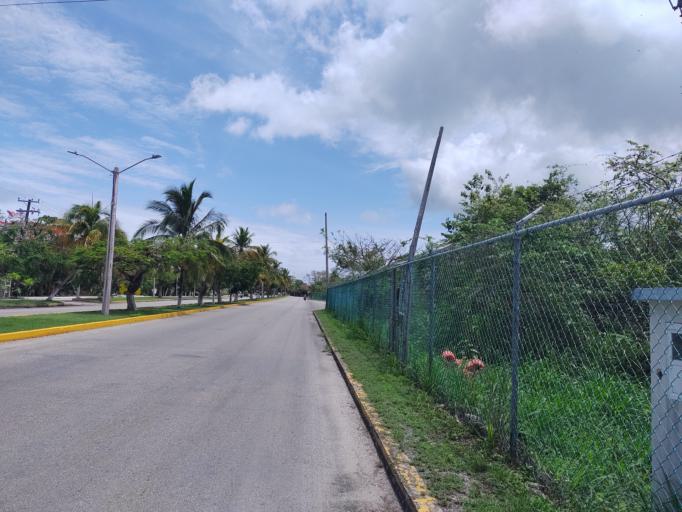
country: MX
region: Quintana Roo
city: San Miguel de Cozumel
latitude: 20.5231
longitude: -86.9422
